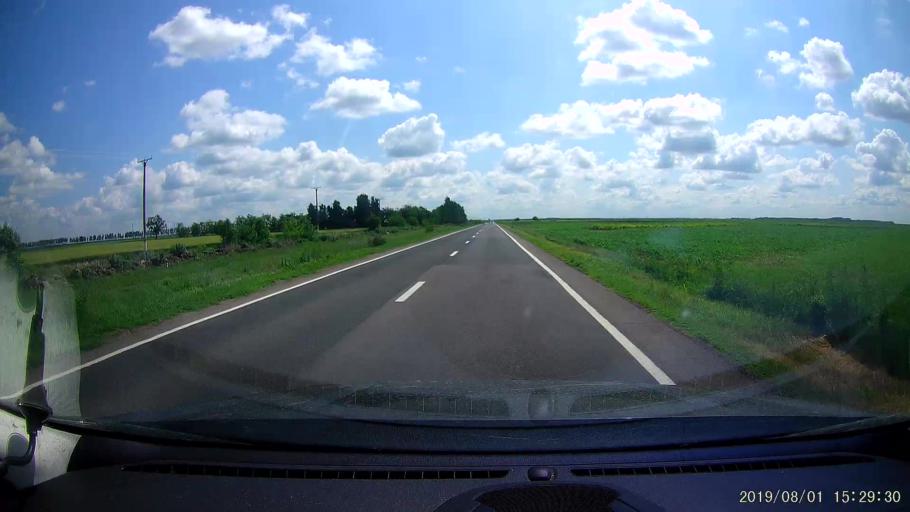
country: RO
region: Braila
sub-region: Comuna Viziru
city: Viziru
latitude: 44.9809
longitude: 27.6956
